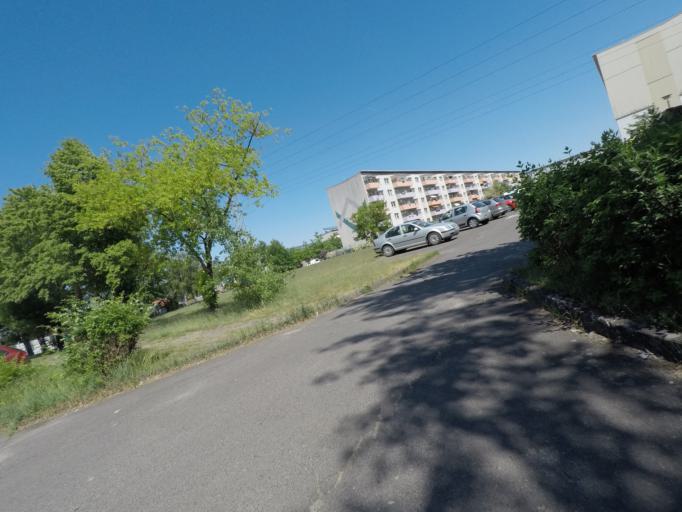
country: DE
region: Brandenburg
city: Melchow
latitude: 52.8361
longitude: 13.7465
